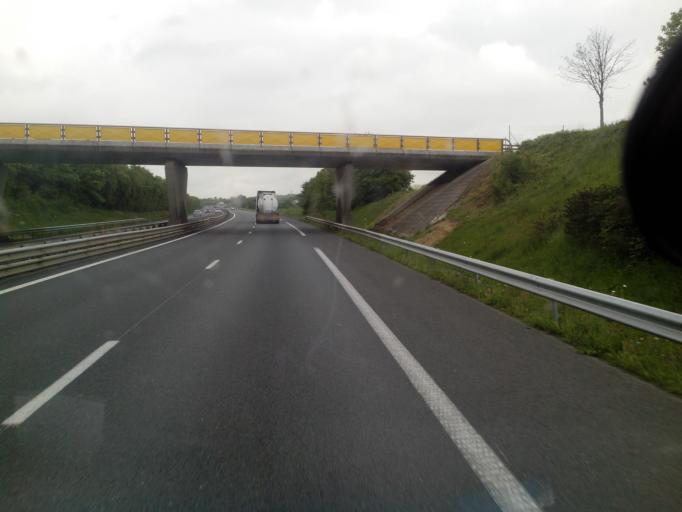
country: FR
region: Lower Normandy
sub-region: Departement du Calvados
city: Villers-Bocage
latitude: 49.0776
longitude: -0.6413
